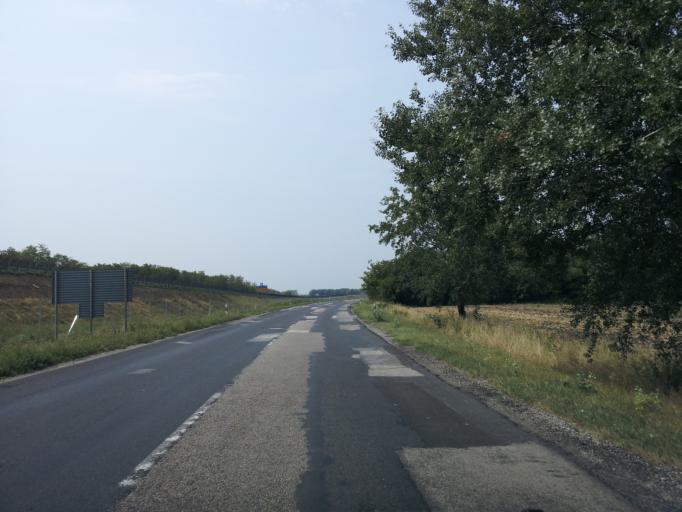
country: HU
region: Gyor-Moson-Sopron
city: Kony
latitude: 47.6247
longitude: 17.3148
